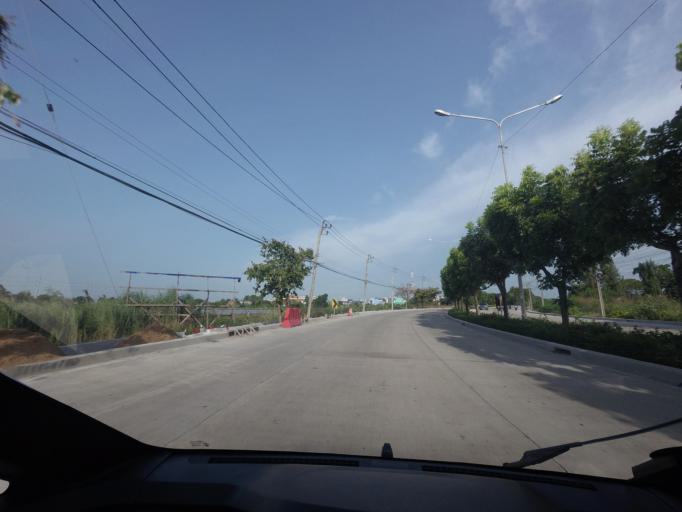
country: TH
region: Samut Prakan
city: Ban Khlong Bang Sao Thong
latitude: 13.7009
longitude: 100.8465
